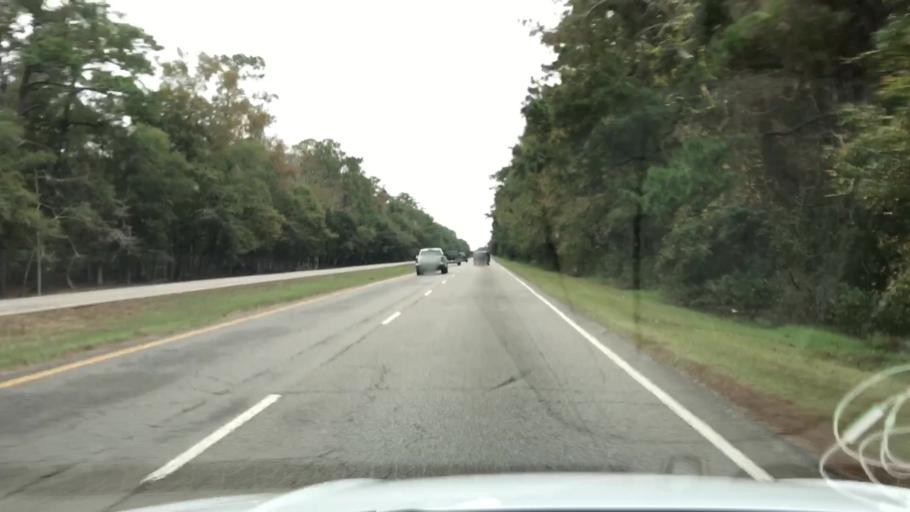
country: US
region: South Carolina
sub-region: Georgetown County
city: Murrells Inlet
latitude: 33.5158
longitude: -79.0718
